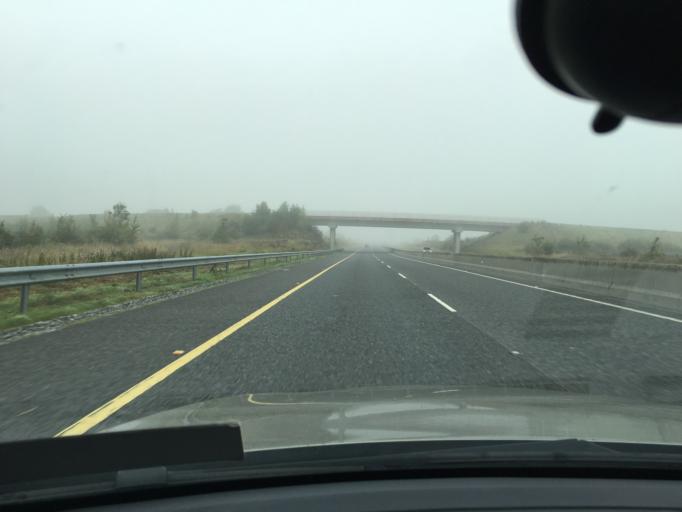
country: IE
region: Leinster
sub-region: An Iarmhi
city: Kilbeggan
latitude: 53.3726
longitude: -7.5436
